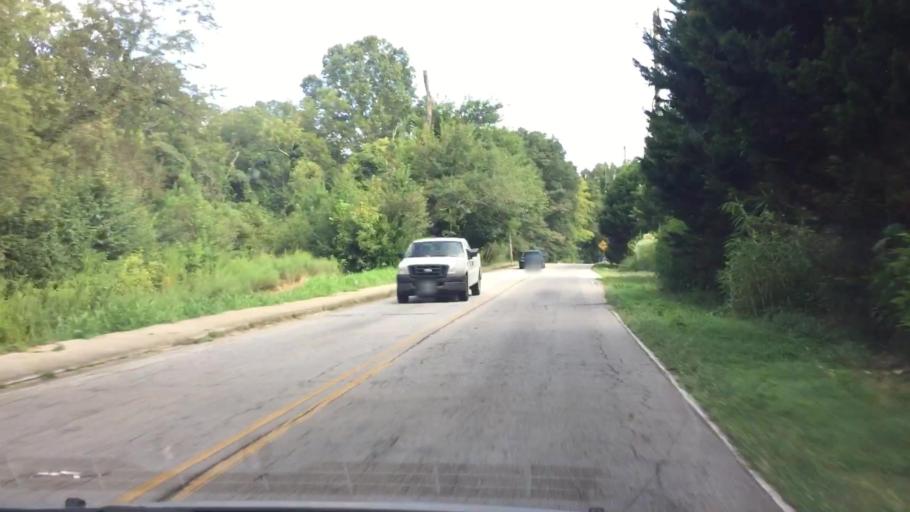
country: US
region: Georgia
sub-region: DeKalb County
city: Gresham Park
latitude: 33.6972
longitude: -84.3238
